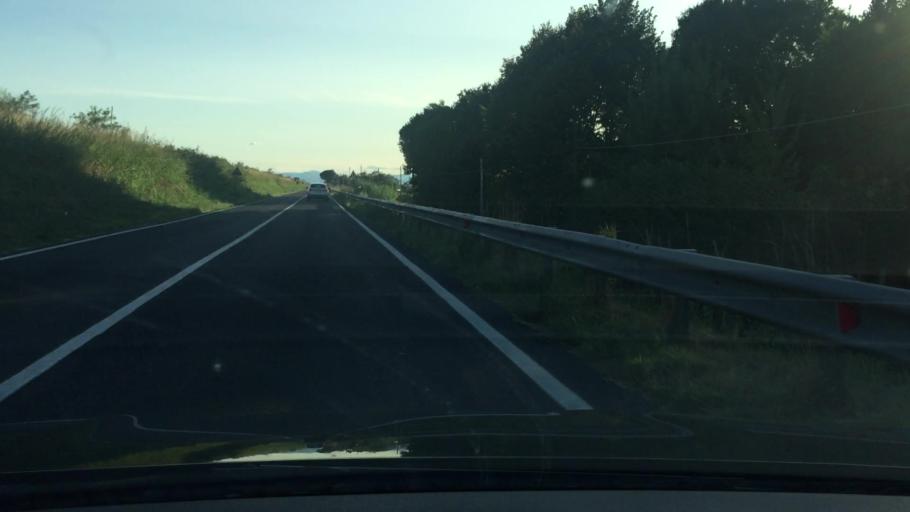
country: IT
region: Emilia-Romagna
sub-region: Provincia di Ravenna
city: Savio
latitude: 44.3016
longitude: 12.2826
